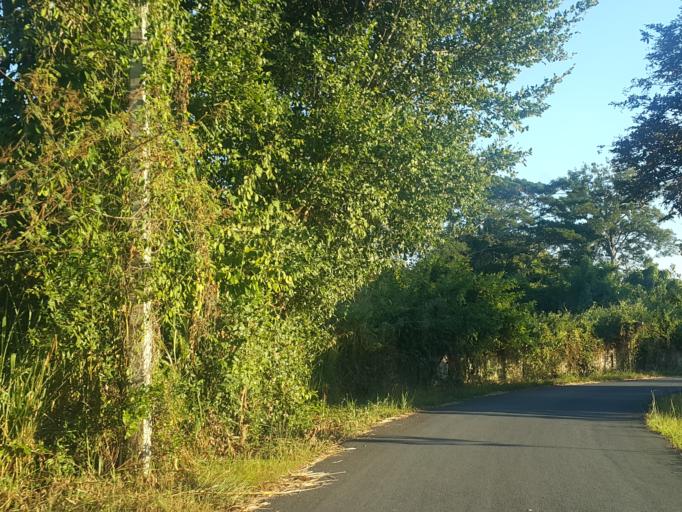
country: TH
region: Chiang Mai
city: San Sai
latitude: 18.8734
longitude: 99.1558
